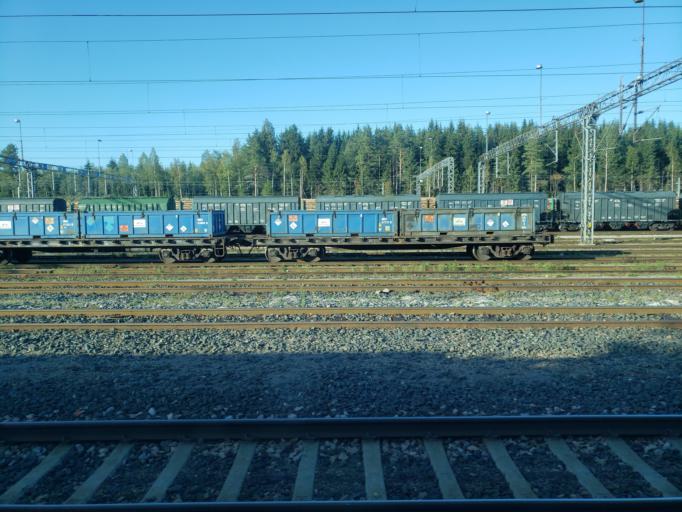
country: FI
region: South Karelia
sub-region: Lappeenranta
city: Lappeenranta
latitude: 60.8619
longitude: 28.3122
